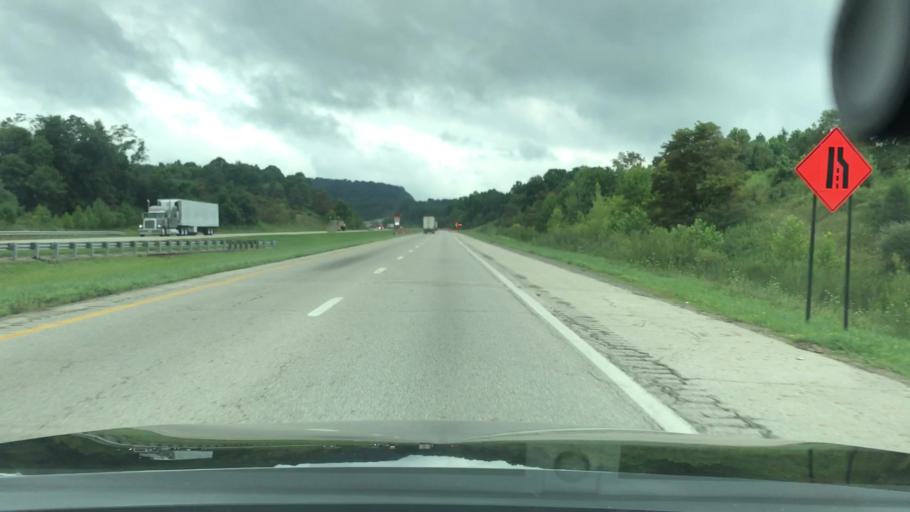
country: US
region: Ohio
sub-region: Ross County
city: Chillicothe
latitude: 39.2490
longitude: -82.8487
